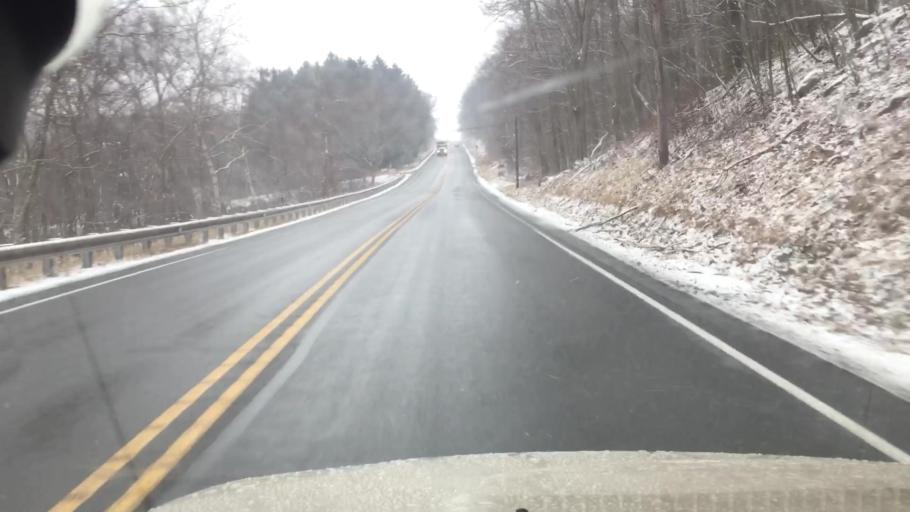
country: US
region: Pennsylvania
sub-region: Luzerne County
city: Conyngham
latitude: 41.0339
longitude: -76.1095
